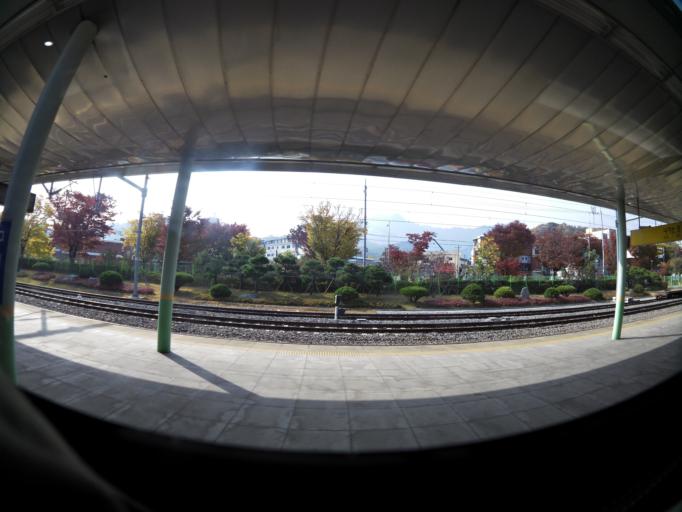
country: KR
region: Gyeongsangbuk-do
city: Gumi
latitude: 36.1274
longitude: 128.3329
